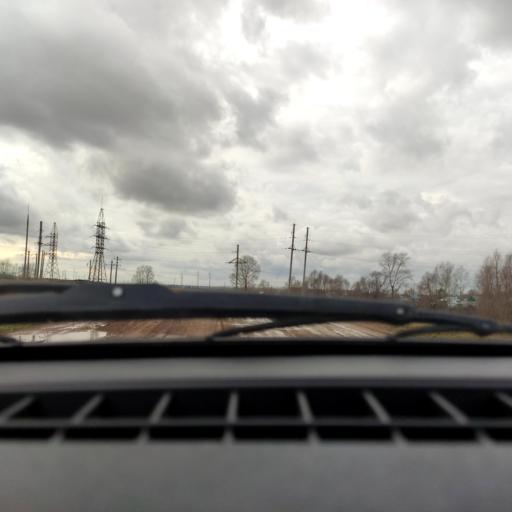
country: RU
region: Bashkortostan
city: Asanovo
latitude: 54.9572
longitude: 55.5630
